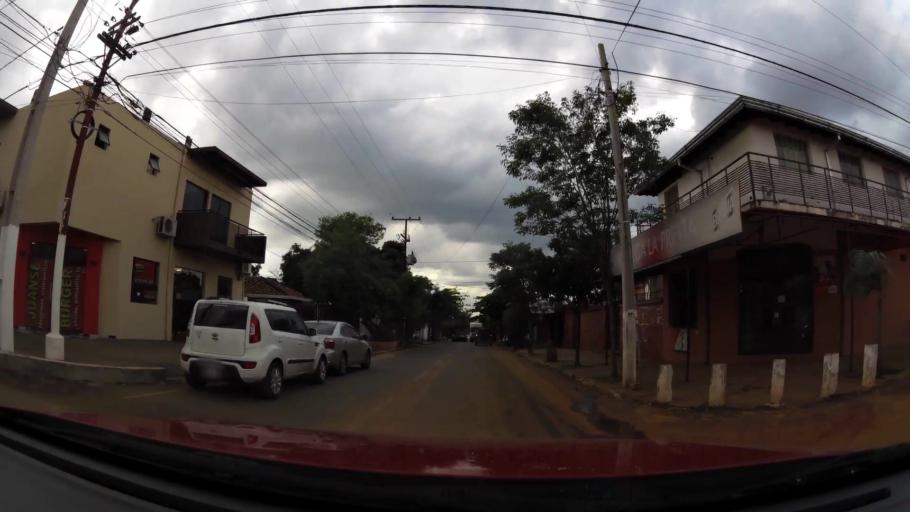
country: PY
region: Central
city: Fernando de la Mora
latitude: -25.3286
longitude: -57.5536
